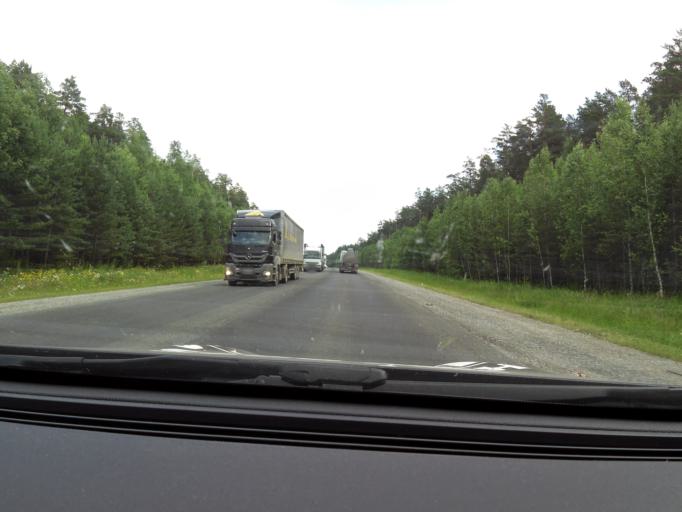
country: RU
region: Sverdlovsk
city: Achit
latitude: 56.7798
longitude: 57.9423
